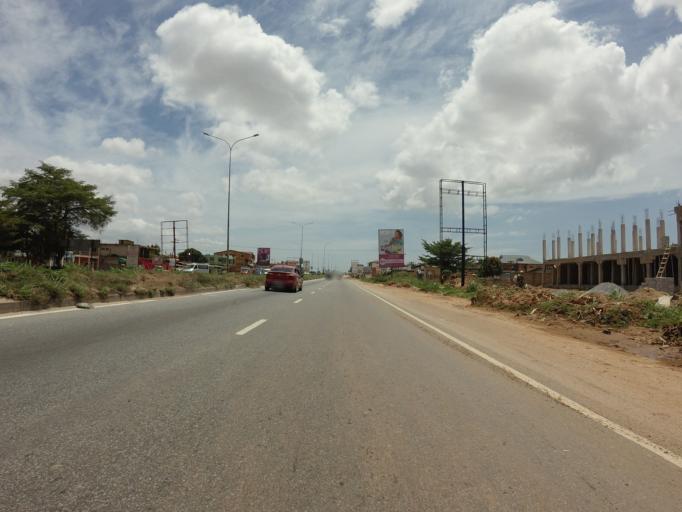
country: GH
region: Greater Accra
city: Gbawe
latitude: 5.5485
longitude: -0.3502
